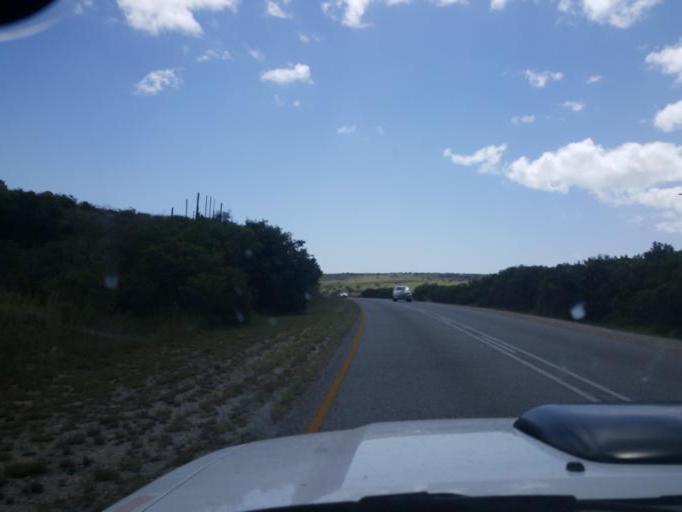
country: ZA
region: Eastern Cape
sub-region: Cacadu District Municipality
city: Grahamstown
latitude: -33.5327
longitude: 26.0551
